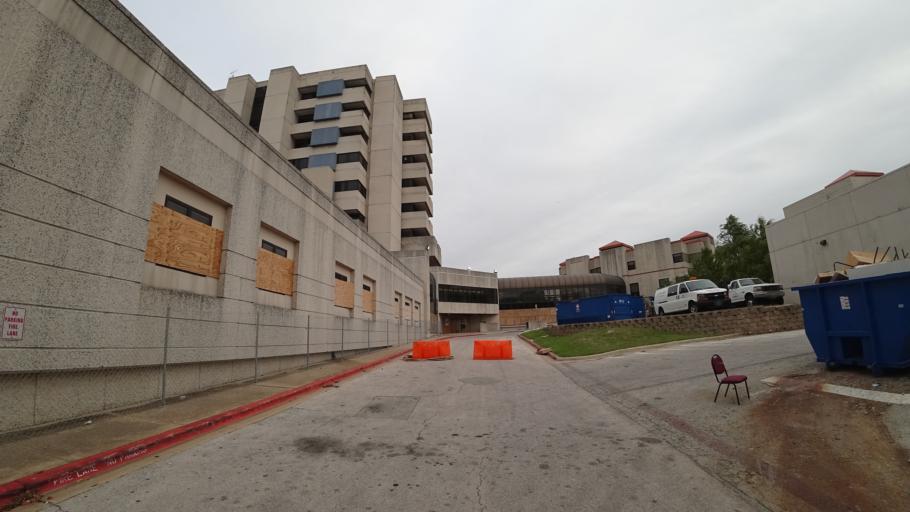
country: US
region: Texas
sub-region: Travis County
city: Austin
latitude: 30.2737
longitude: -97.7333
